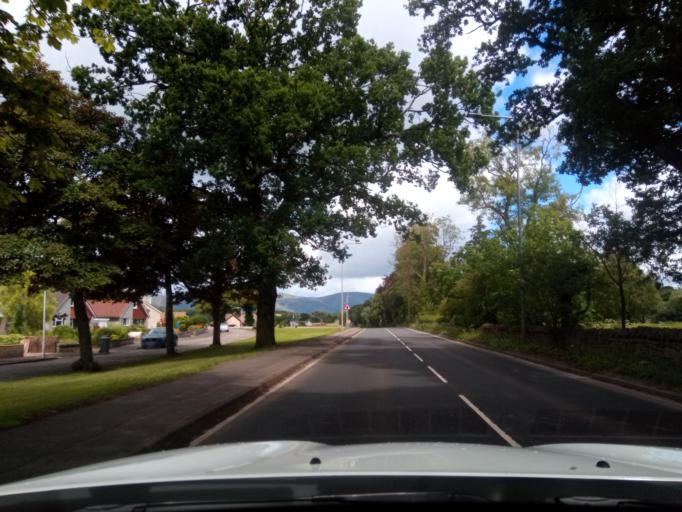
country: GB
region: Scotland
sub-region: Fife
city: Kincardine
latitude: 56.0784
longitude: -3.7204
